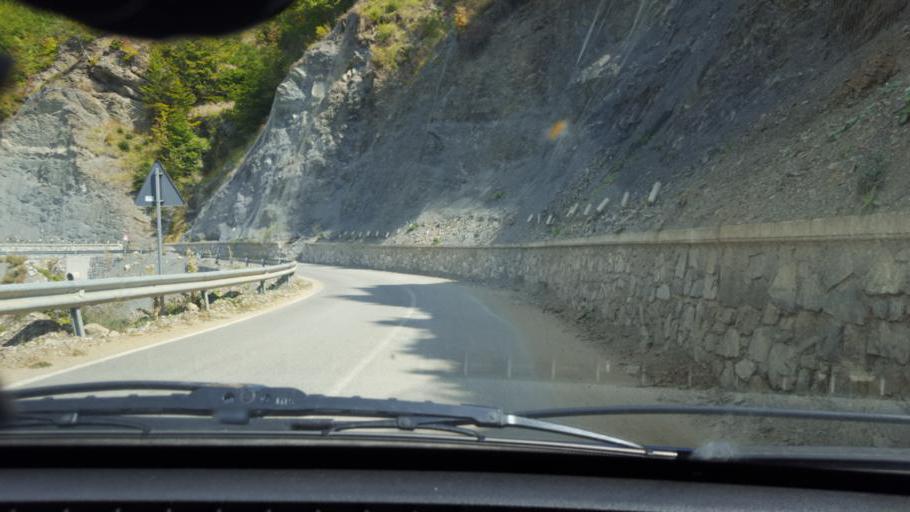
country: AL
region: Kukes
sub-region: Rrethi i Tropojes
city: Valbone
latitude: 42.5378
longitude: 19.7014
